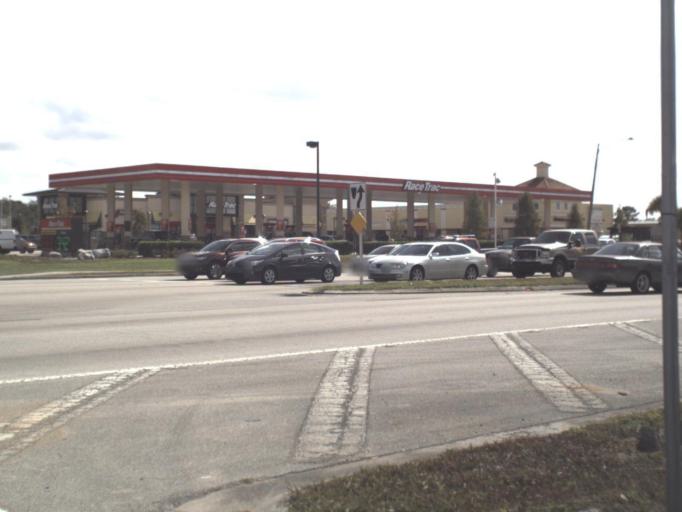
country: US
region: Florida
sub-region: Osceola County
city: Poinciana
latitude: 28.1543
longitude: -81.4402
